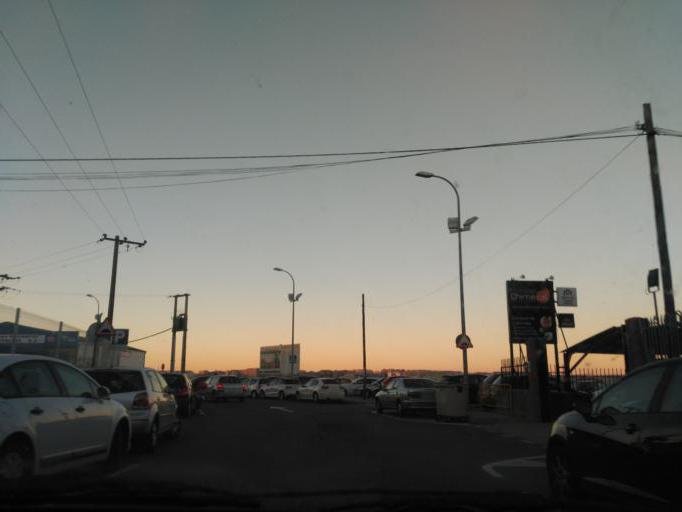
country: ES
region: Castille and Leon
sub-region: Provincia de Salamanca
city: Carbajosa de la Sagrada
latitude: 40.9473
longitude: -5.6530
